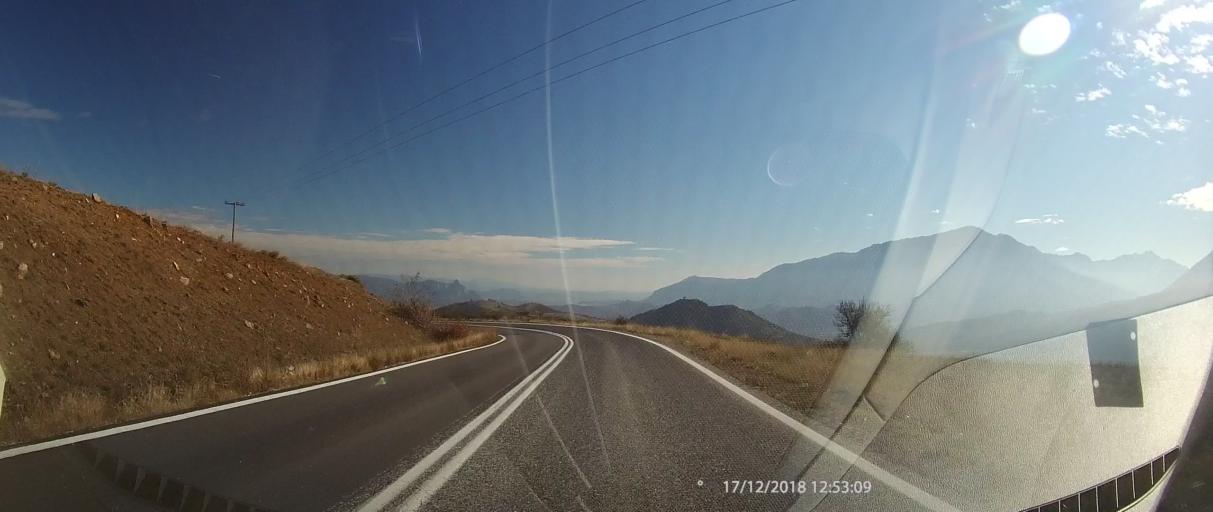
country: GR
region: Thessaly
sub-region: Trikala
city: Kastraki
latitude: 39.7563
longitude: 21.4873
